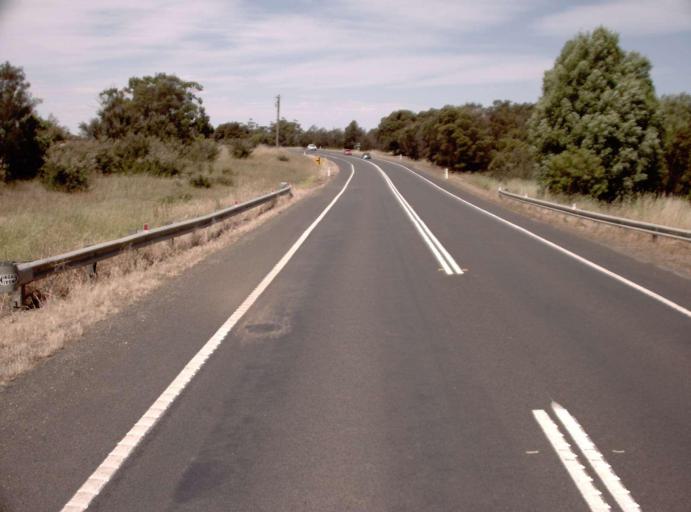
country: AU
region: Victoria
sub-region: Wellington
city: Heyfield
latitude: -38.1316
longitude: 146.8177
